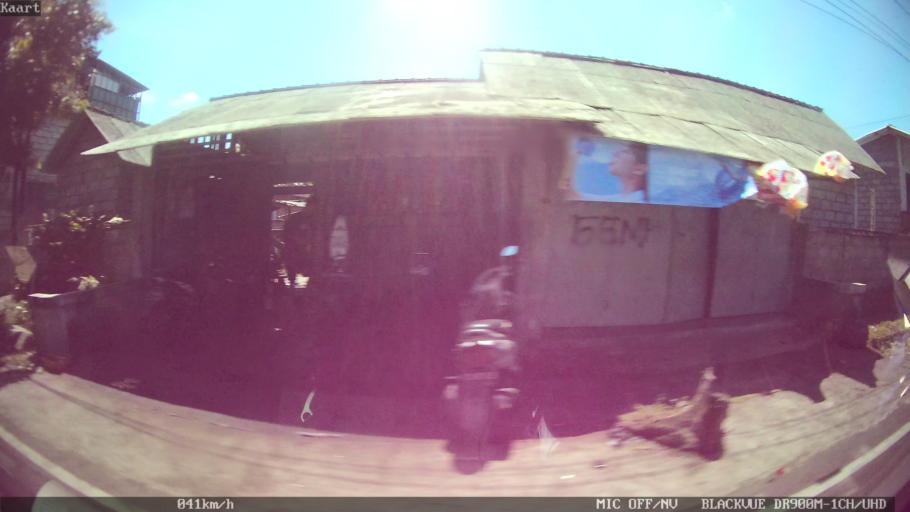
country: ID
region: Bali
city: Banjar Pasekan
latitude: -8.5720
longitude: 115.3306
